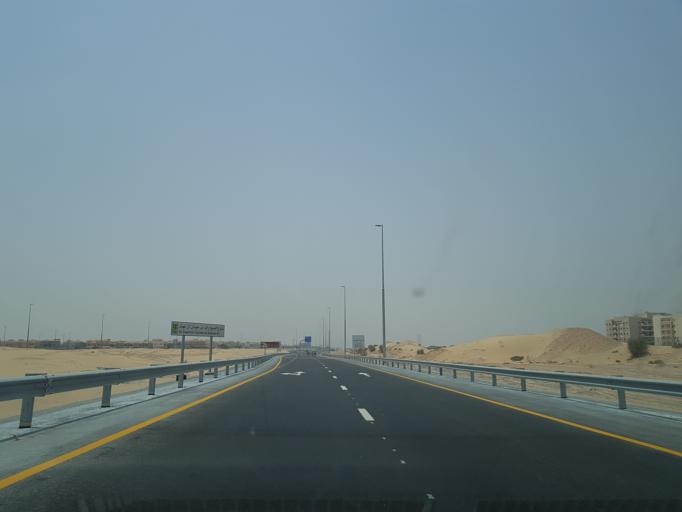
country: AE
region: Dubai
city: Dubai
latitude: 25.1012
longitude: 55.3740
